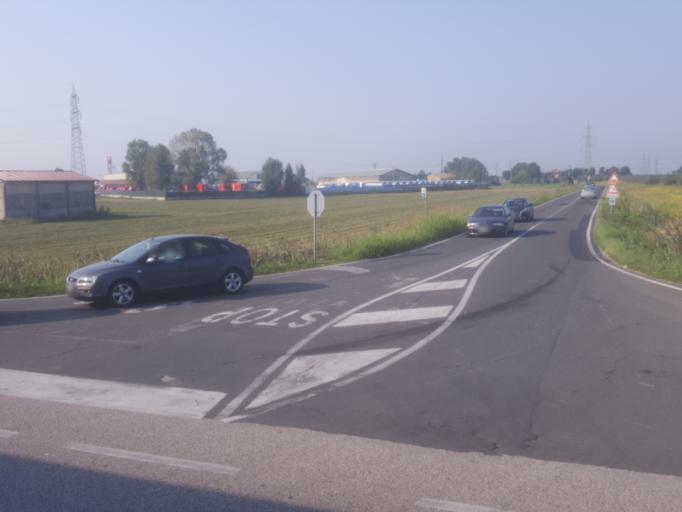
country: IT
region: Emilia-Romagna
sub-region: Provincia di Ravenna
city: Fornace Zarattini
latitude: 44.4314
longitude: 12.1502
